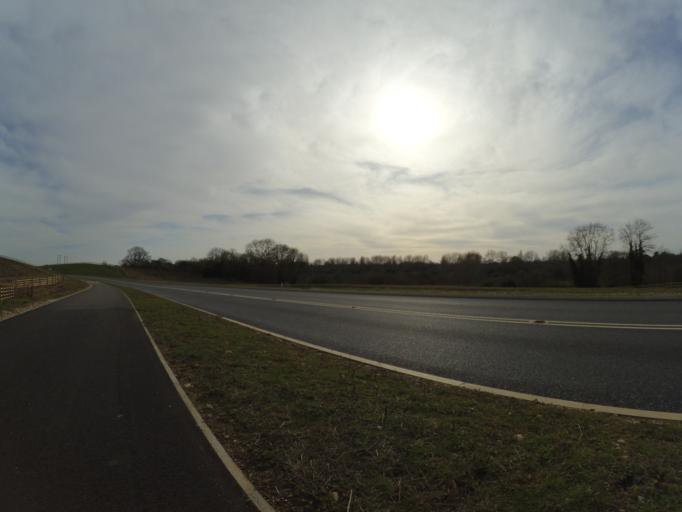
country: GB
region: England
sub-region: Warwickshire
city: Rugby
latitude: 52.3725
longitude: -1.2248
